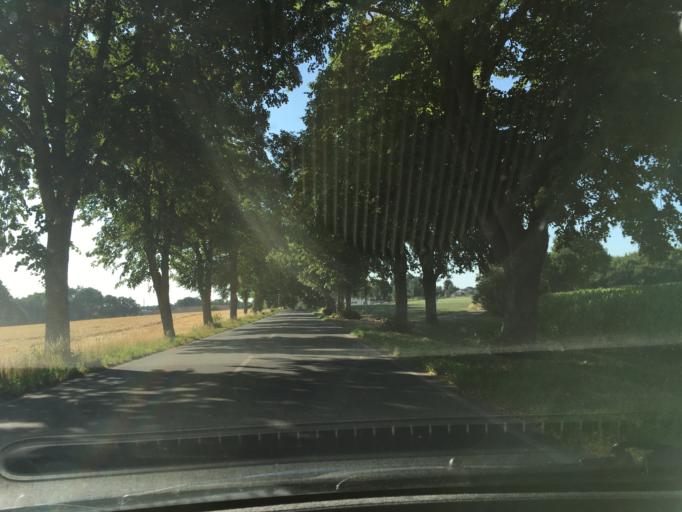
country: DE
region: Lower Saxony
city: Dahlem
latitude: 53.1809
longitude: 10.7584
